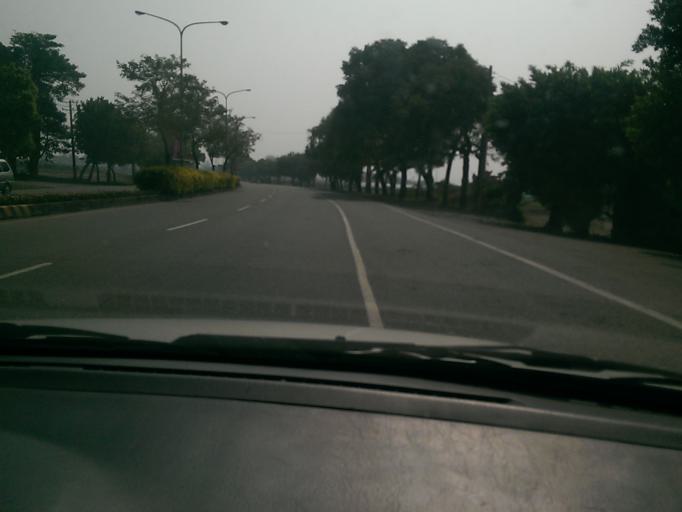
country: TW
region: Taiwan
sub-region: Yunlin
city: Douliu
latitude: 23.7720
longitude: 120.4807
